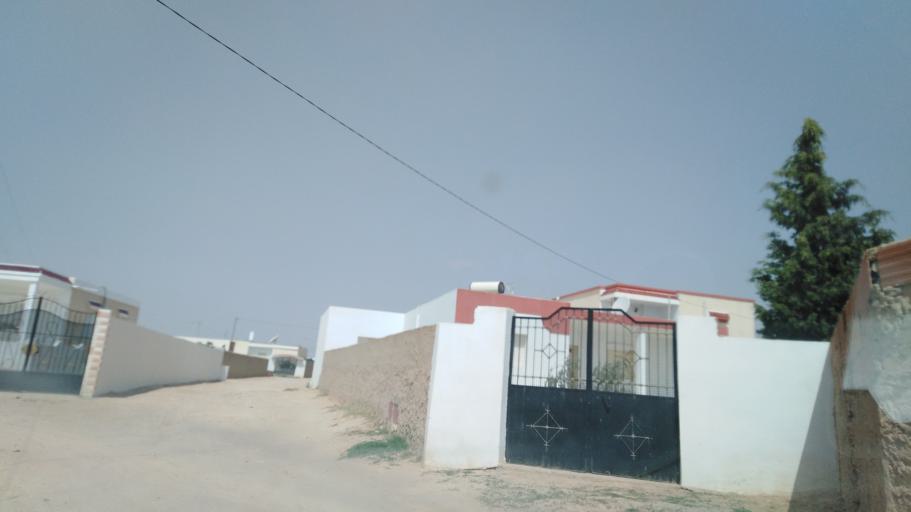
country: TN
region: Safaqis
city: Sfax
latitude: 34.6262
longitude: 10.5748
